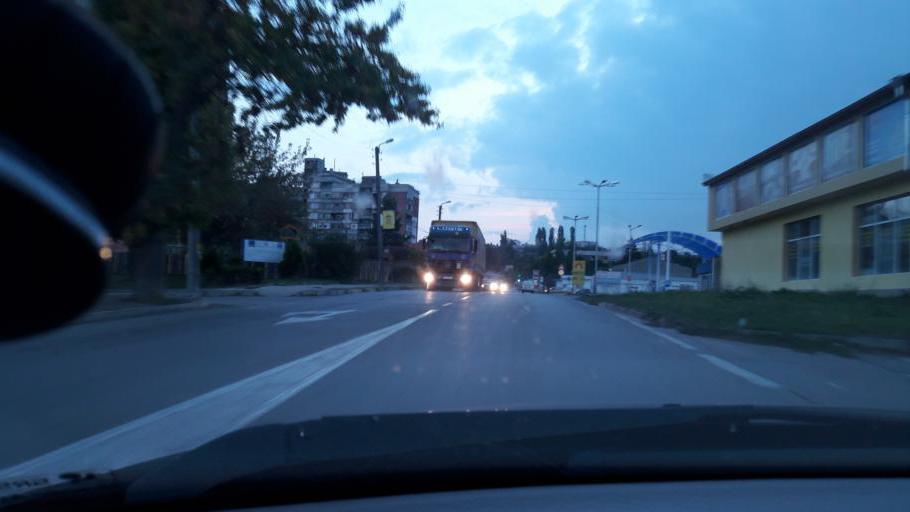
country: BG
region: Razgrad
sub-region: Obshtina Razgrad
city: Razgrad
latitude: 43.5304
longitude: 26.5133
